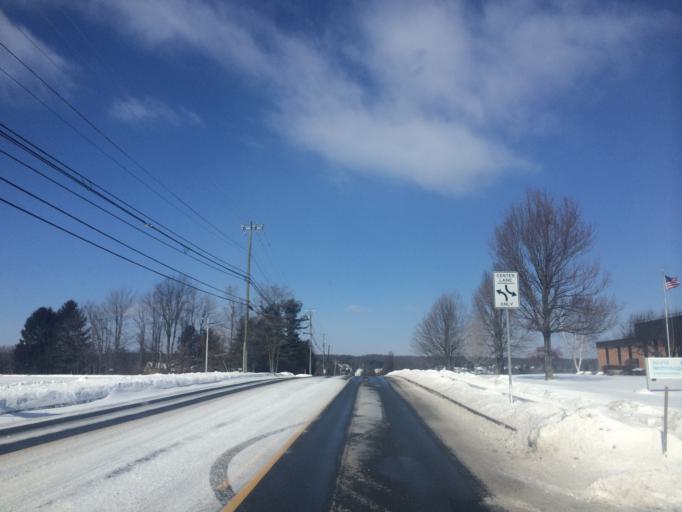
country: US
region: Pennsylvania
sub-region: Centre County
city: Park Forest Village
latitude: 40.7812
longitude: -77.8987
